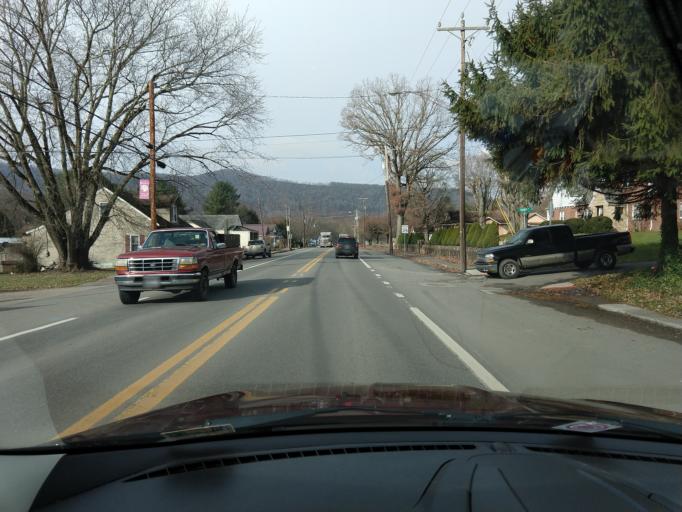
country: US
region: West Virginia
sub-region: Greenbrier County
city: Rainelle
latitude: 37.9639
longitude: -80.6938
